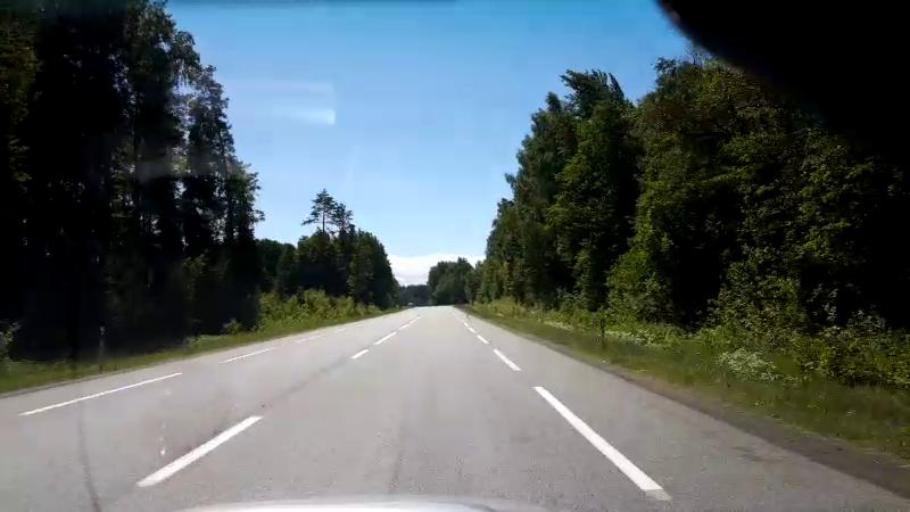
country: LV
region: Saulkrastu
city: Saulkrasti
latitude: 57.4198
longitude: 24.4287
